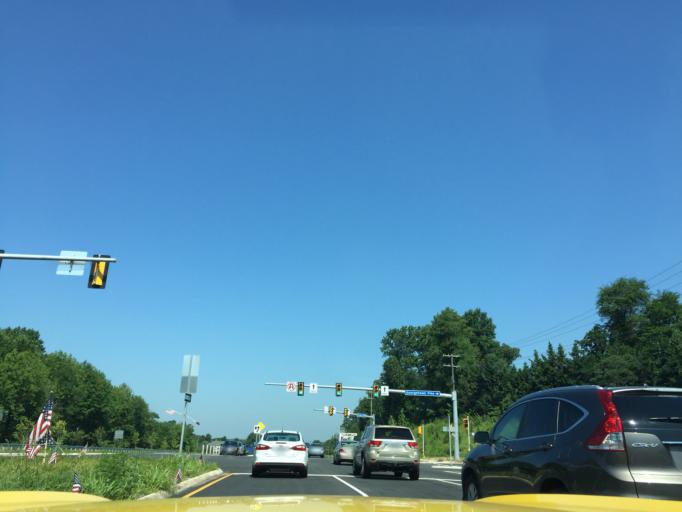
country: US
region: Virginia
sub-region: Fairfax County
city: Dranesville
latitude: 39.0004
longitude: -77.3448
